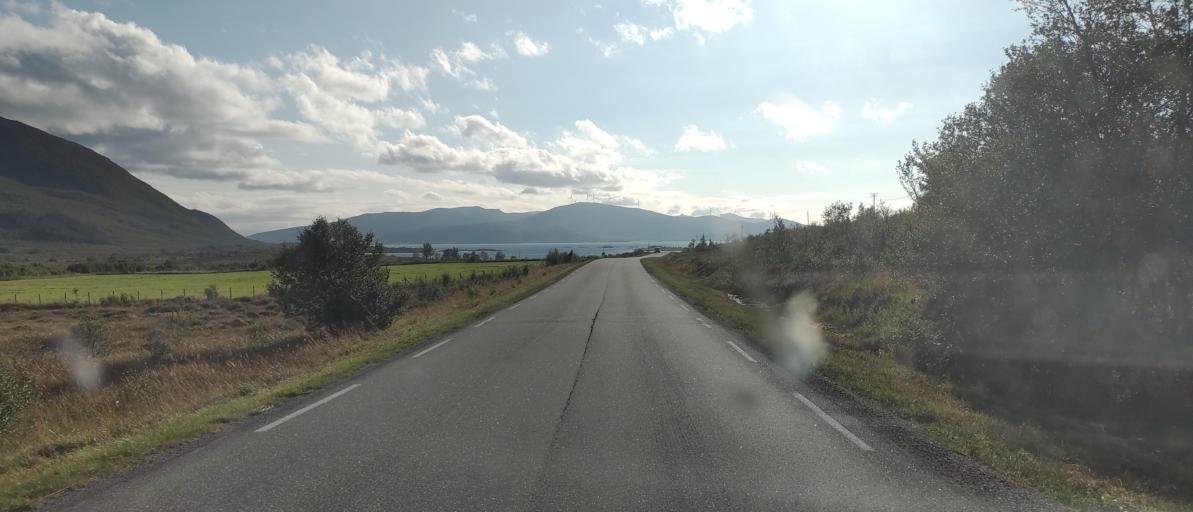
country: NO
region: Nordland
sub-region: Sortland
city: Sortland
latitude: 68.7901
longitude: 15.5006
